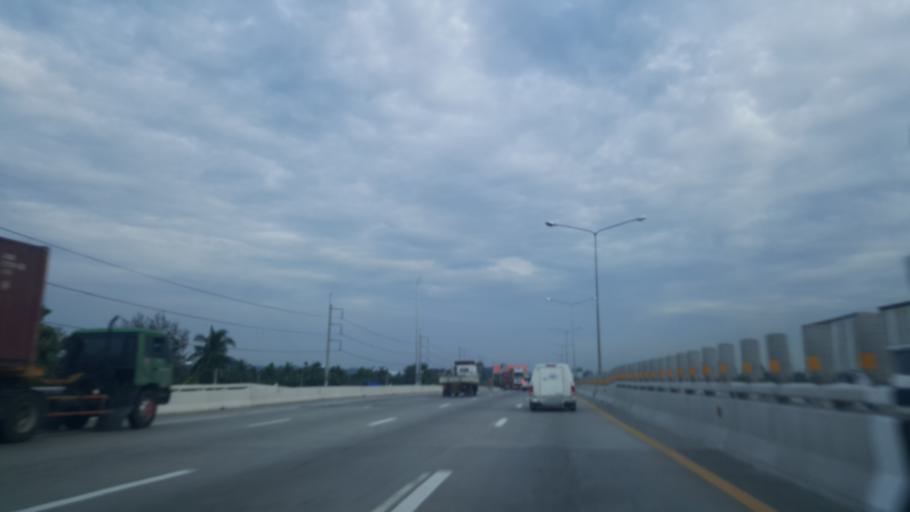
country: TH
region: Chon Buri
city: Si Racha
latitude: 13.2307
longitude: 101.0007
